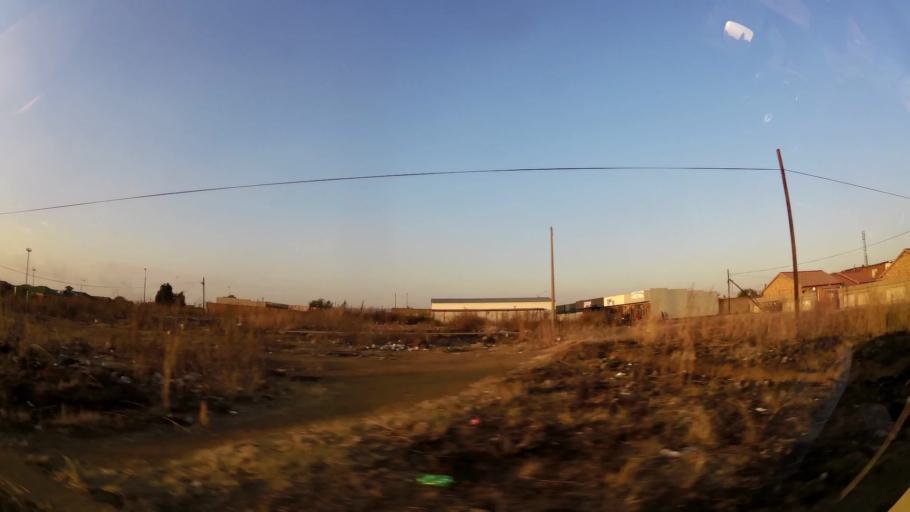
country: ZA
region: Gauteng
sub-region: West Rand District Municipality
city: Randfontein
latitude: -26.2038
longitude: 27.7043
